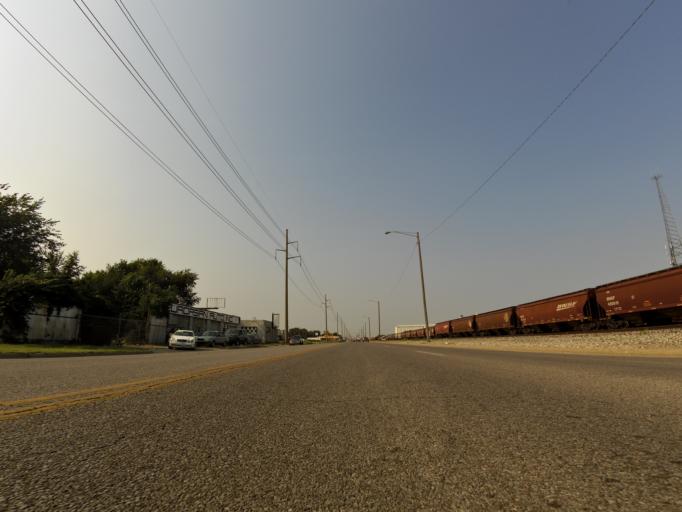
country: US
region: Kansas
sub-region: Sedgwick County
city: Wichita
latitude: 37.7338
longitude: -97.3358
